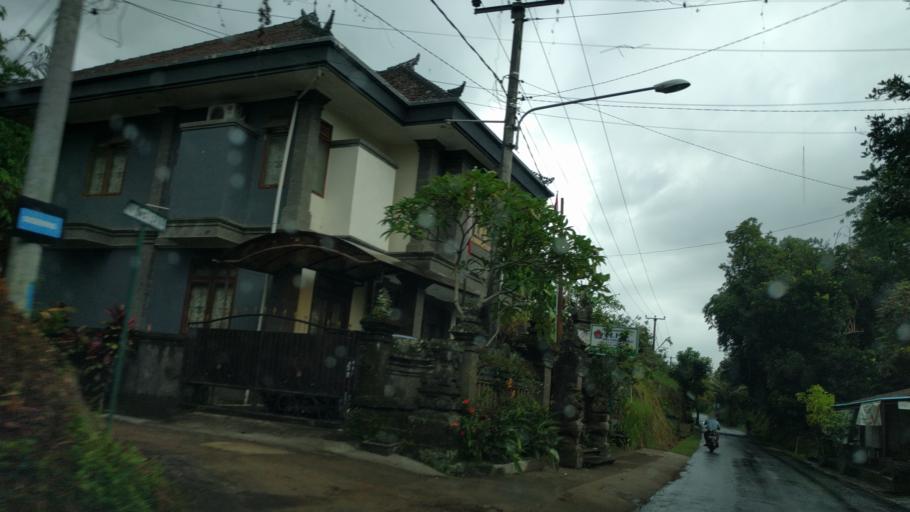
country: ID
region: Bali
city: Bunutan
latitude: -8.4736
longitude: 115.2597
